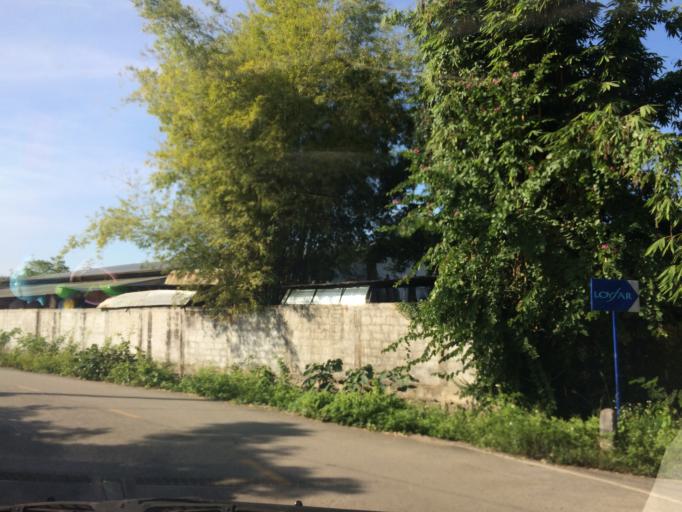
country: TH
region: Chiang Mai
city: Saraphi
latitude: 18.7273
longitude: 99.0087
